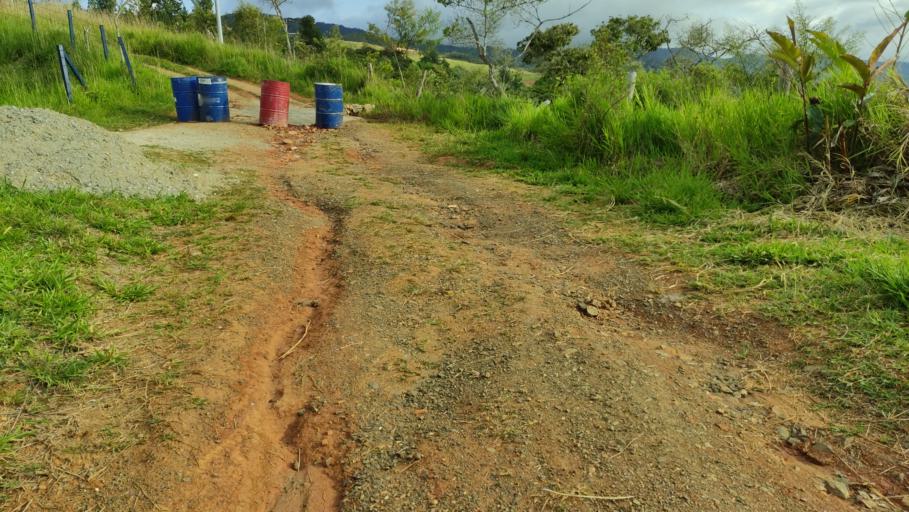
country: CO
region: Valle del Cauca
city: Dagua
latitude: 3.5362
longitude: -76.6431
